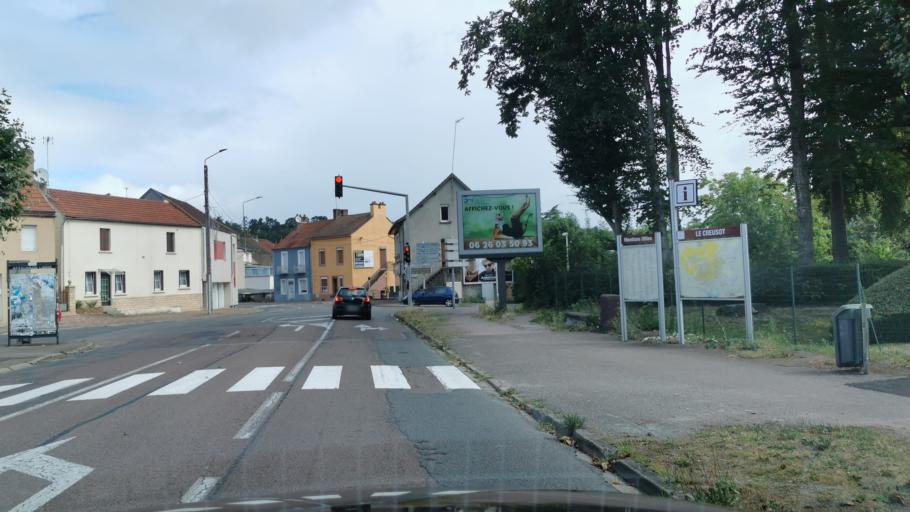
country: FR
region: Bourgogne
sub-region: Departement de Saone-et-Loire
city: Le Creusot
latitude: 46.8027
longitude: 4.4130
